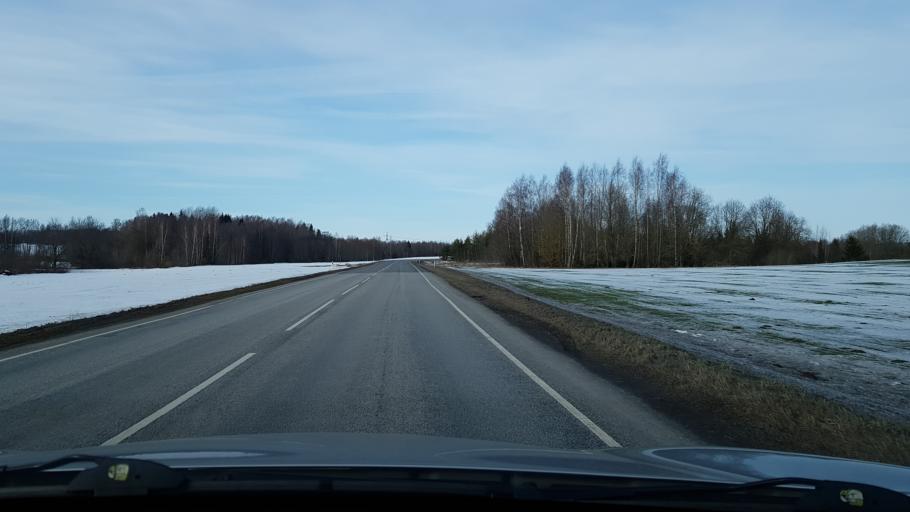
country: EE
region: Viljandimaa
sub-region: Viljandi linn
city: Viljandi
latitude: 58.3413
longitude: 25.4683
